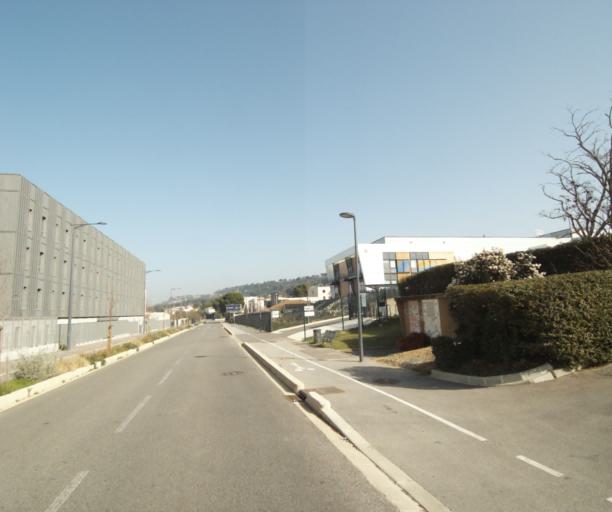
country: FR
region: Provence-Alpes-Cote d'Azur
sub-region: Departement des Bouches-du-Rhone
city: Vitrolles
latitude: 43.4449
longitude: 5.2335
